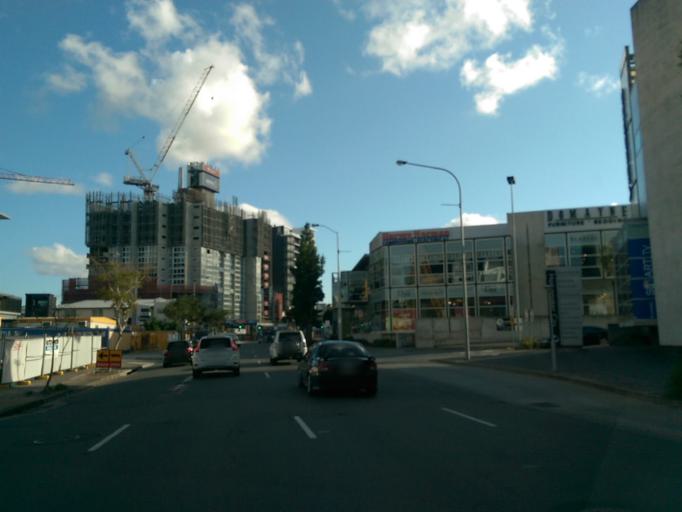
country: AU
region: Queensland
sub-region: Brisbane
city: Fortitude Valley
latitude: -27.4513
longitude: 153.0410
